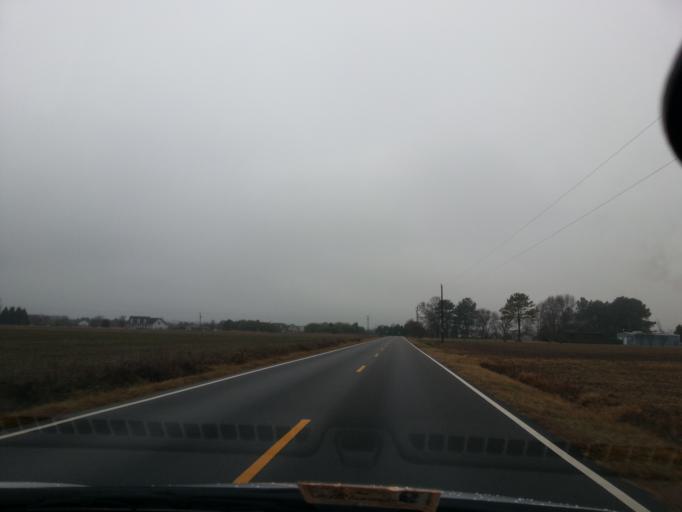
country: US
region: North Carolina
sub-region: Currituck County
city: Moyock
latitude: 36.4958
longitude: -76.1946
